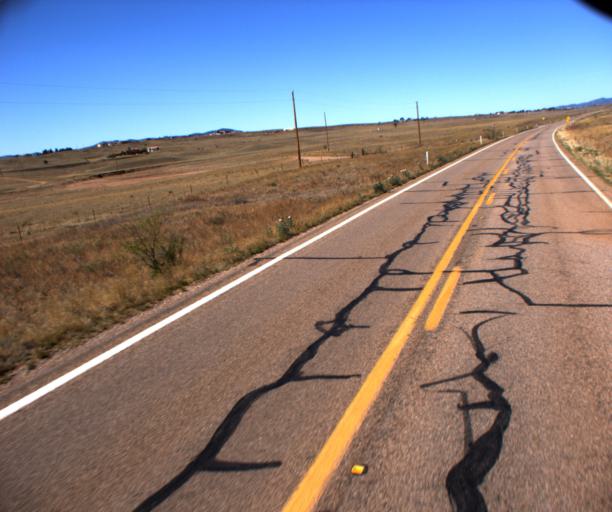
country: US
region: Arizona
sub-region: Cochise County
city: Huachuca City
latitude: 31.6855
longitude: -110.6204
